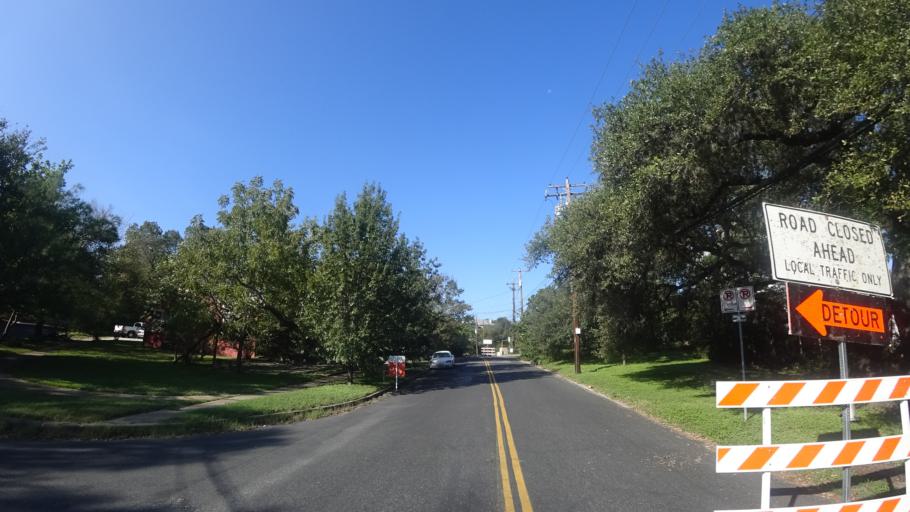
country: US
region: Texas
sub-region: Travis County
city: Austin
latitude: 30.2519
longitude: -97.7452
